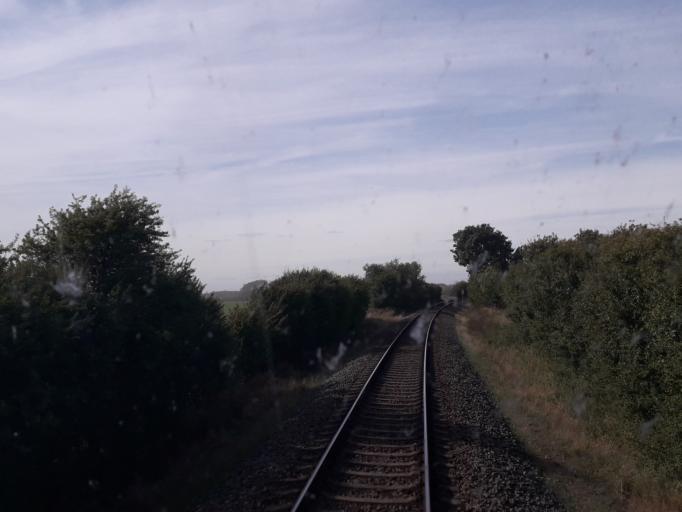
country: DE
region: Brandenburg
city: Neuruppin
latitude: 52.8726
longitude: 12.8612
